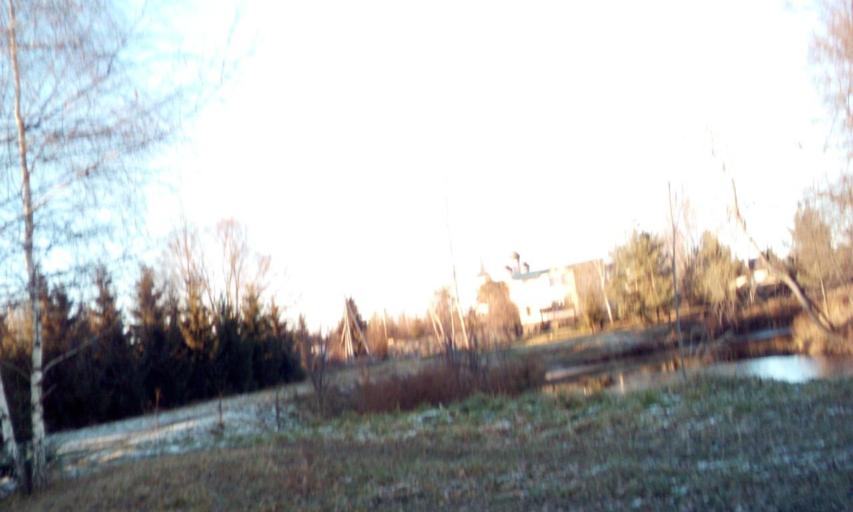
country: RU
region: Moskovskaya
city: Selyatino
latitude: 55.5389
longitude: 36.9996
